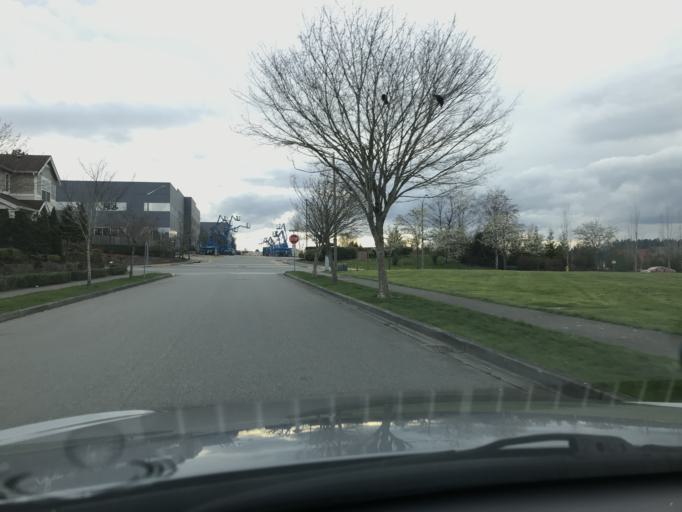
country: US
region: Washington
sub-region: King County
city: Sammamish
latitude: 47.6664
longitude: -122.0867
